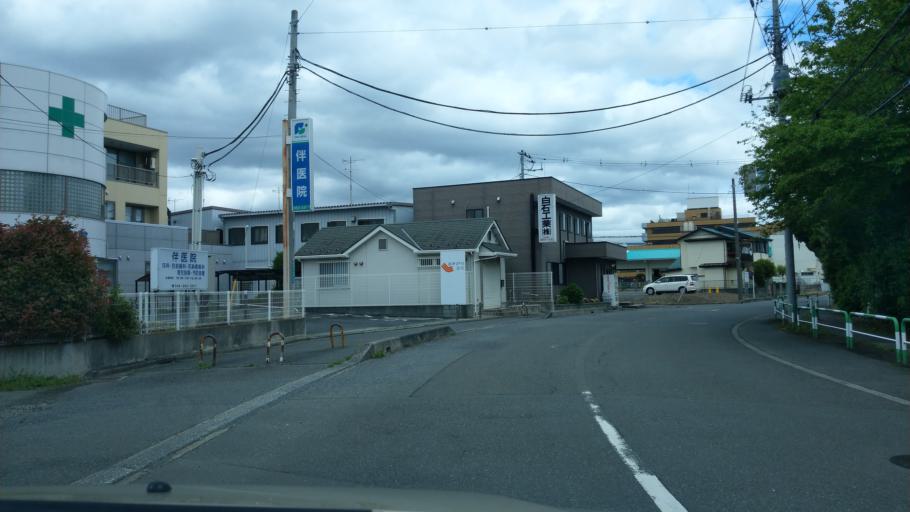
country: JP
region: Saitama
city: Yono
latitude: 35.8461
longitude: 139.6233
